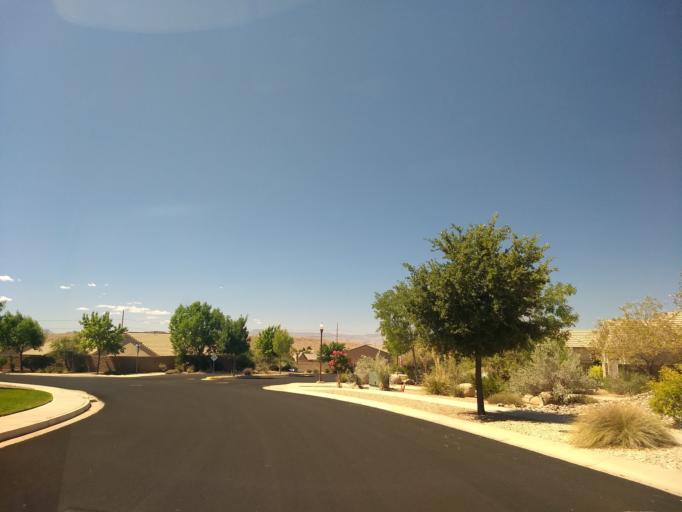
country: US
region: Utah
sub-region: Washington County
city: Washington
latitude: 37.1407
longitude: -113.4697
